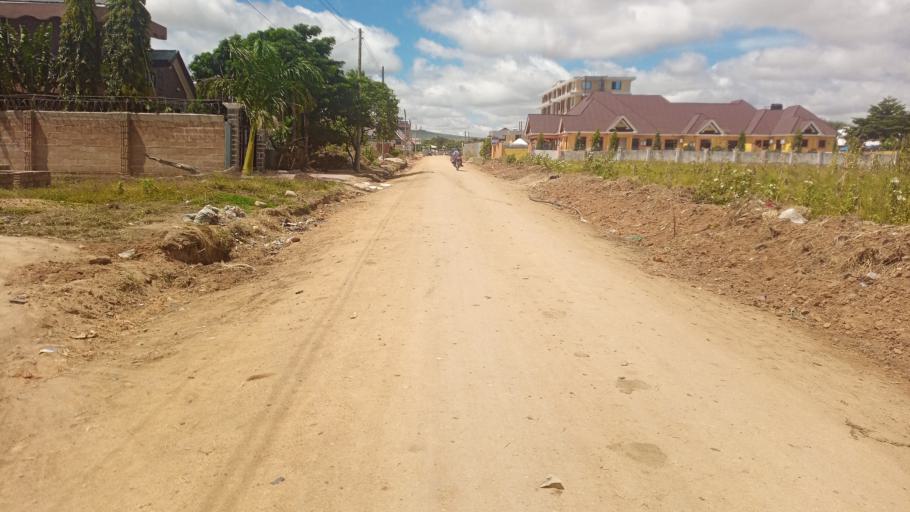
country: TZ
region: Dodoma
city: Dodoma
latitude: -6.1766
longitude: 35.7652
